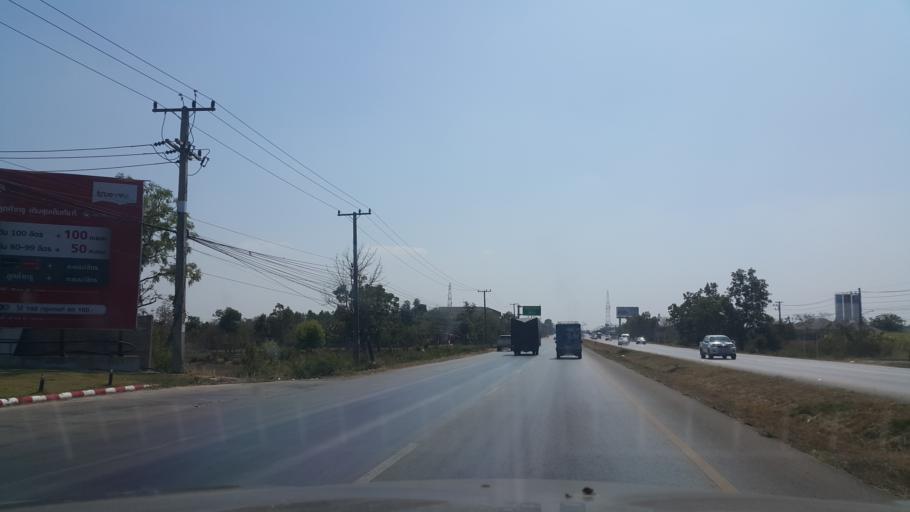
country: TH
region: Changwat Udon Thani
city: Non Sa-at
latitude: 16.9878
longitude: 102.8930
